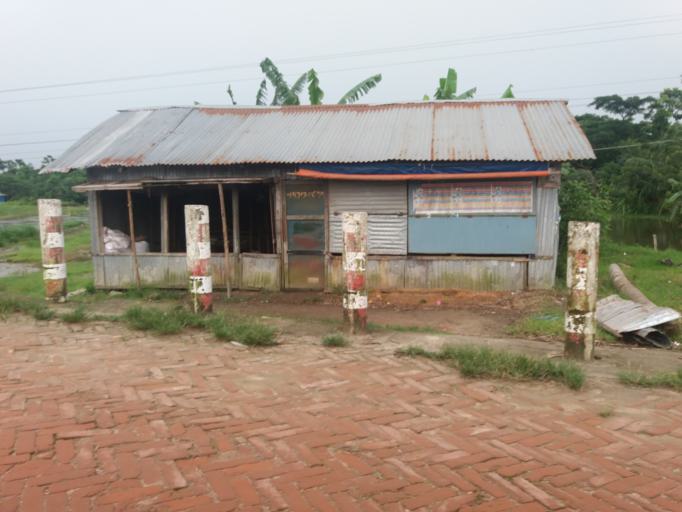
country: BD
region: Chittagong
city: Feni
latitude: 22.9361
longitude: 91.3732
